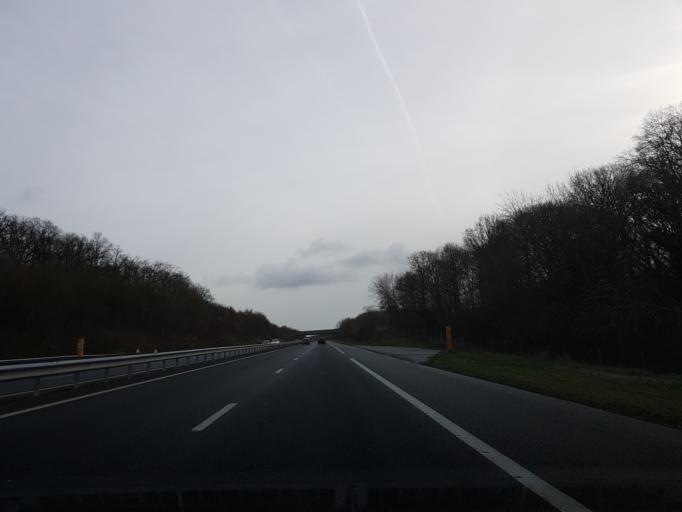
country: FR
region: Bourgogne
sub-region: Departement de l'Yonne
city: Soucy
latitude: 48.2408
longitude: 3.3669
